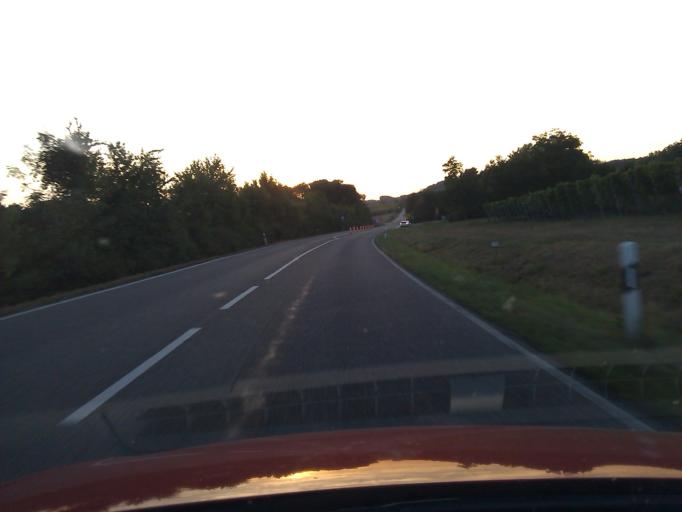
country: DE
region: Baden-Wuerttemberg
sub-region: Regierungsbezirk Stuttgart
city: Brackenheim
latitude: 49.0896
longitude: 9.0527
